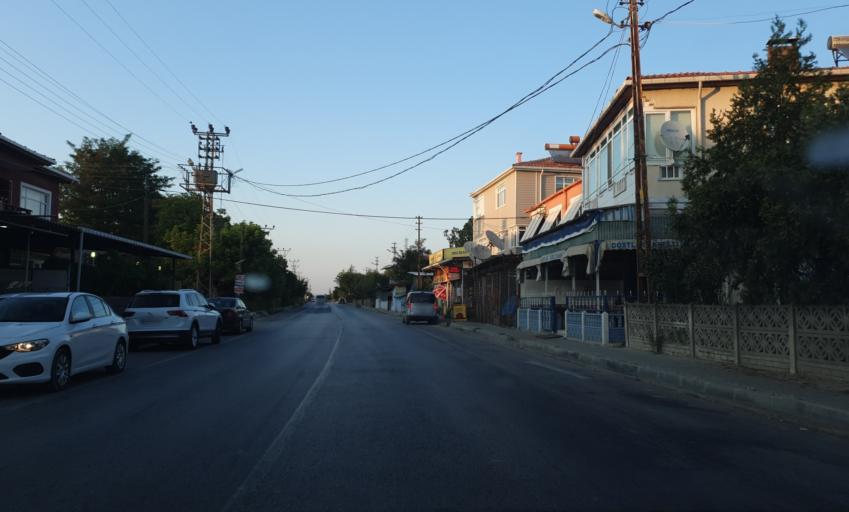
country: TR
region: Kirklareli
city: Luleburgaz
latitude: 41.4607
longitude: 27.3893
